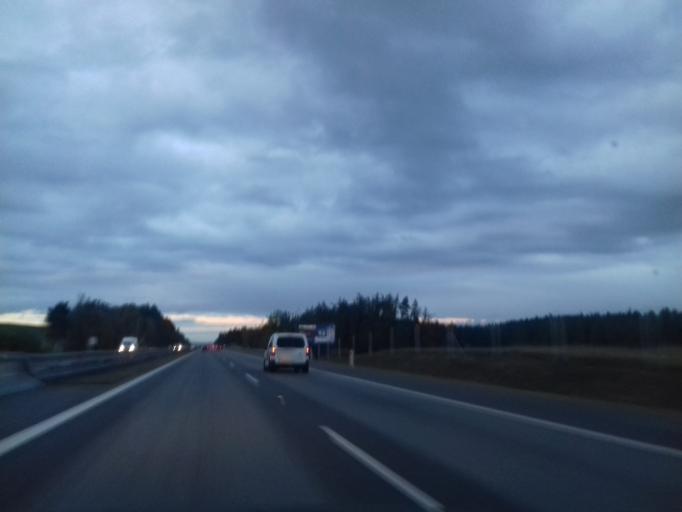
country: CZ
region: Central Bohemia
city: Cechtice
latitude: 49.6371
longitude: 15.1275
